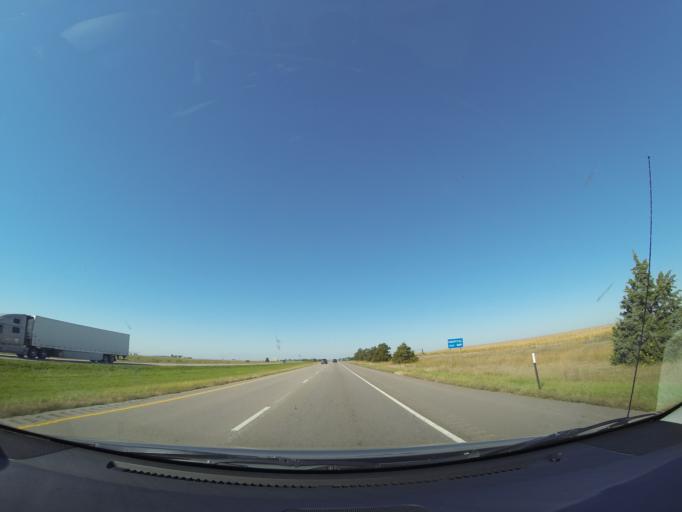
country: US
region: Nebraska
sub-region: Saline County
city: Friend
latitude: 40.8224
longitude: -97.2756
